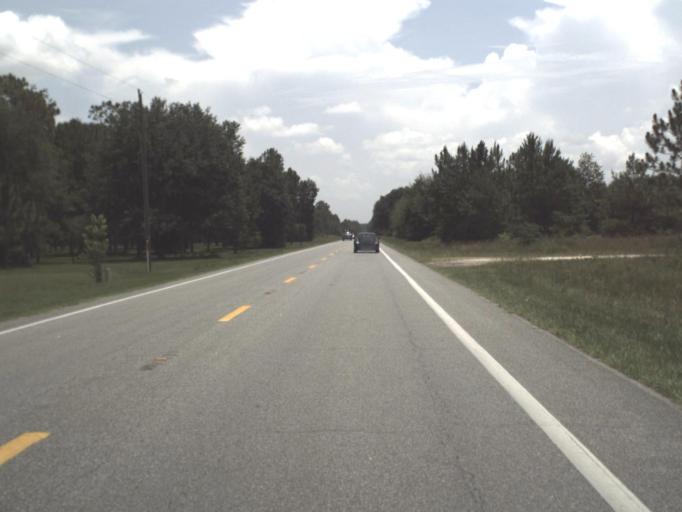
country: US
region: Florida
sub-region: Madison County
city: Madison
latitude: 30.4028
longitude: -83.2263
